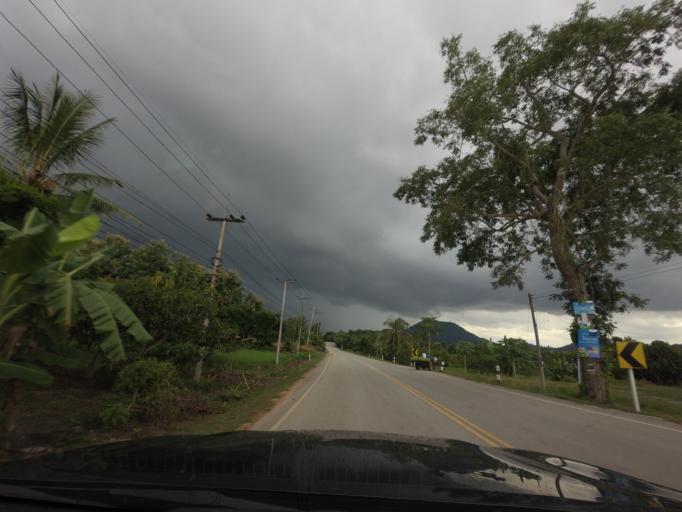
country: LA
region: Vientiane
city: Muang Sanakham
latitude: 17.9552
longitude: 101.7407
